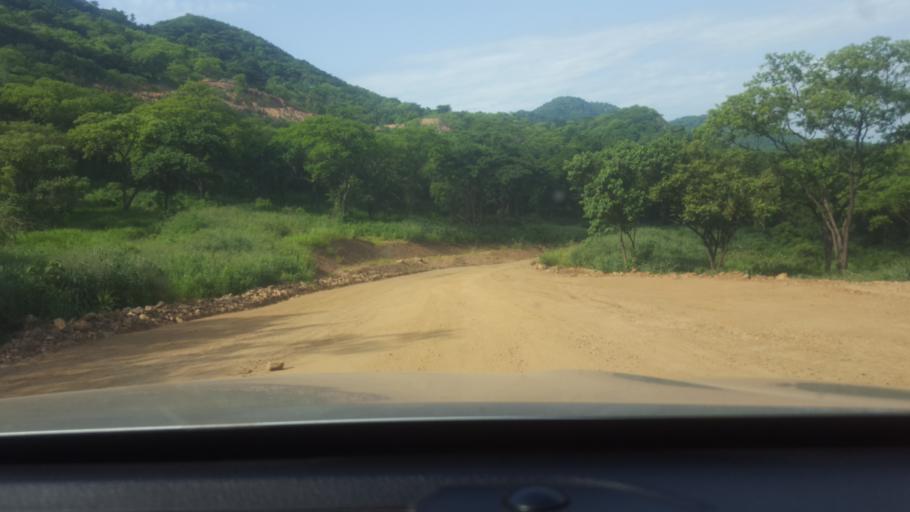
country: ET
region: Southern Nations, Nationalities, and People's Region
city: Tippi
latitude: 7.5416
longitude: 34.9719
